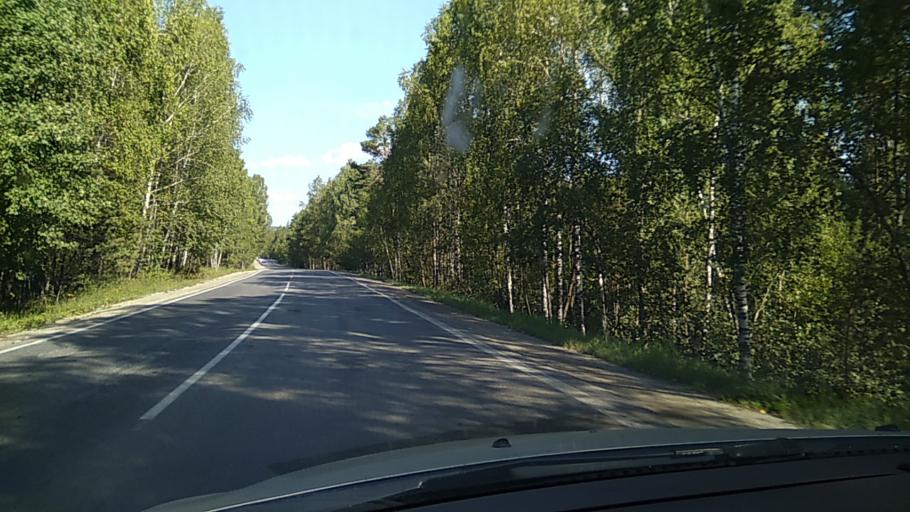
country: RU
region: Chelyabinsk
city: Turgoyak
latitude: 55.1168
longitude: 60.0990
